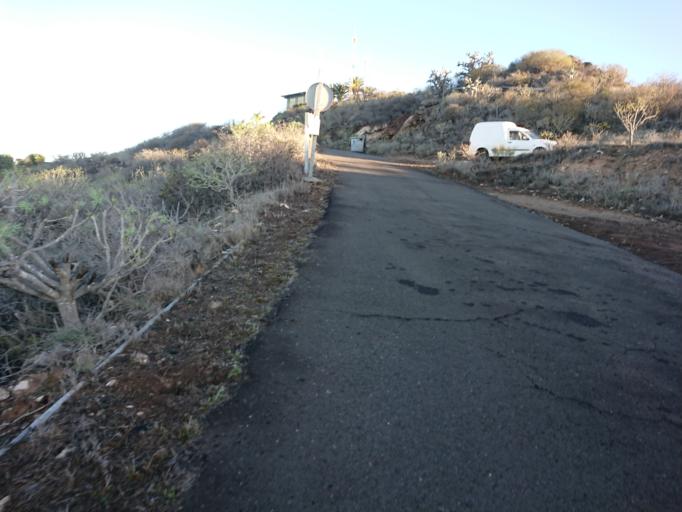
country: ES
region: Canary Islands
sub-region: Provincia de Santa Cruz de Tenerife
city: Tazacorte
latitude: 28.6621
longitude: -17.9431
